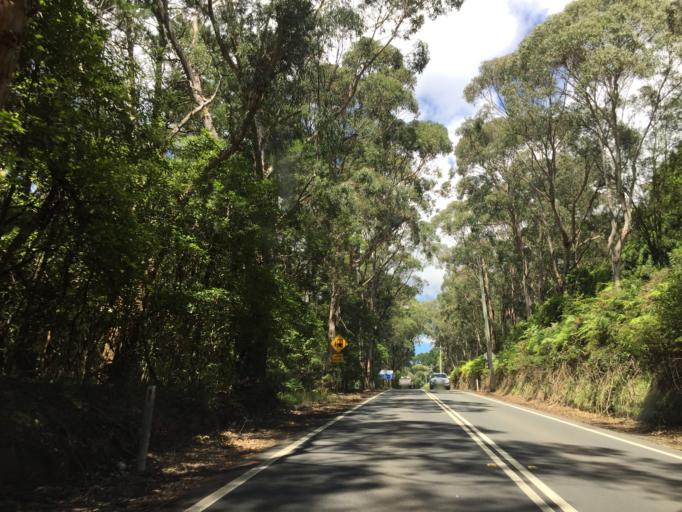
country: AU
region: New South Wales
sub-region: Blue Mountains Municipality
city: Lawson
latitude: -33.5327
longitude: 150.4456
